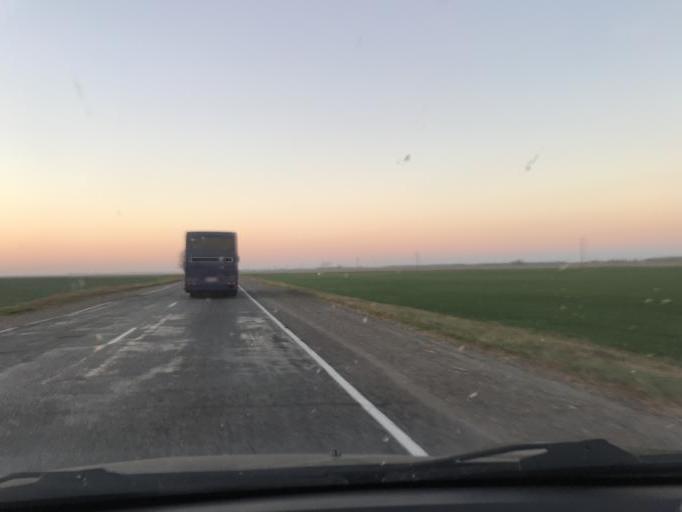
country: BY
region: Gomel
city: Horad Rechytsa
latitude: 52.2194
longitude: 30.5217
